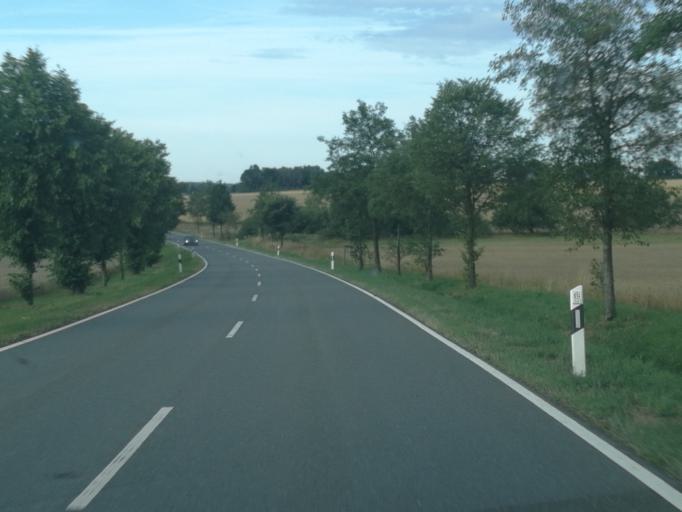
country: DE
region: Bavaria
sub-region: Upper Franconia
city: Regnitzlosau
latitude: 50.3338
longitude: 12.0703
